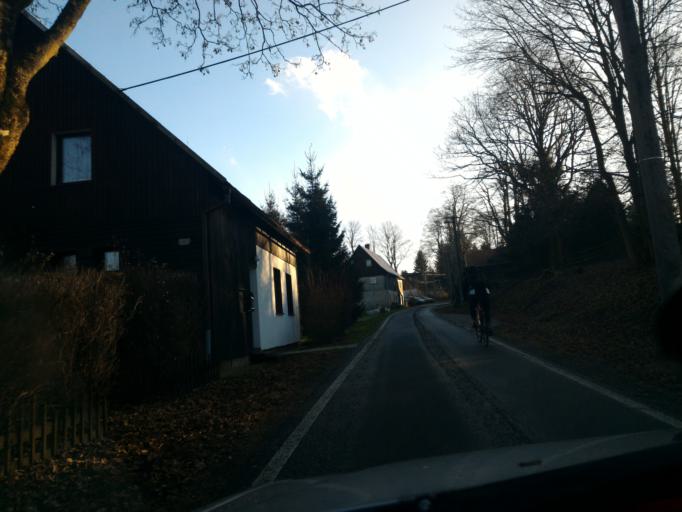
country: DE
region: Saxony
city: Kurort Jonsdorf
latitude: 50.8355
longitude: 14.7080
